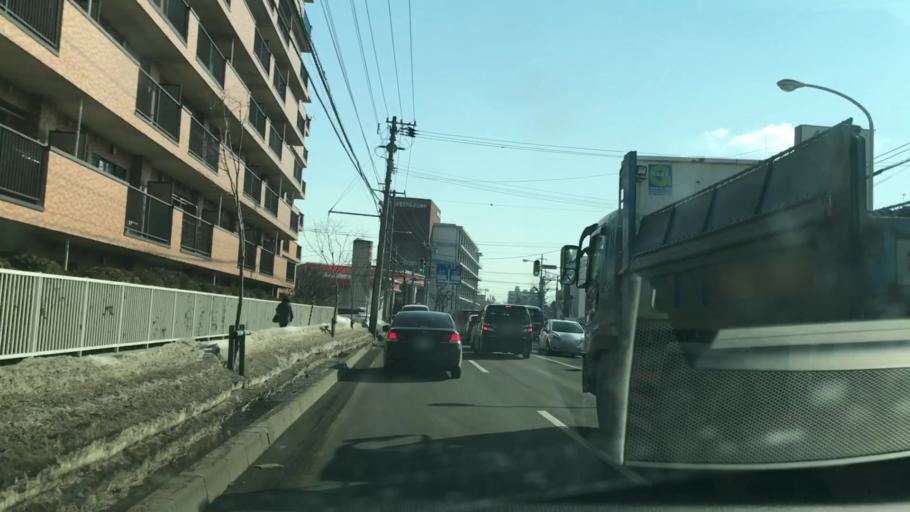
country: JP
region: Hokkaido
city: Sapporo
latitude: 43.0252
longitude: 141.3791
